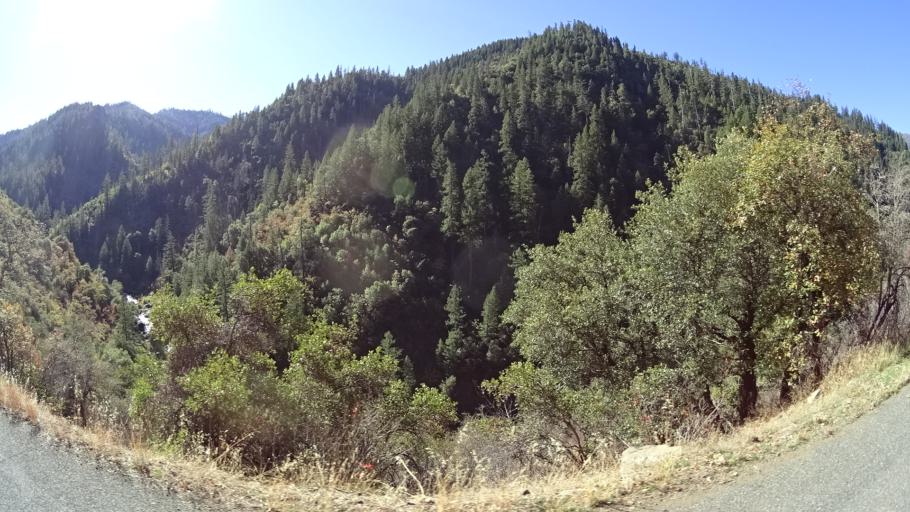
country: US
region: California
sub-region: Humboldt County
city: Willow Creek
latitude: 41.1480
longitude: -123.2030
